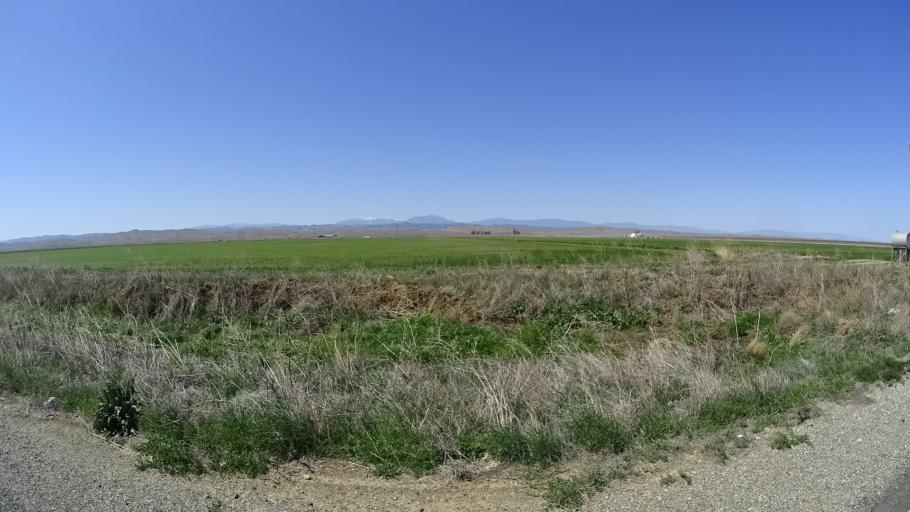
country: US
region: California
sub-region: Glenn County
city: Willows
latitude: 39.4323
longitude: -122.2486
